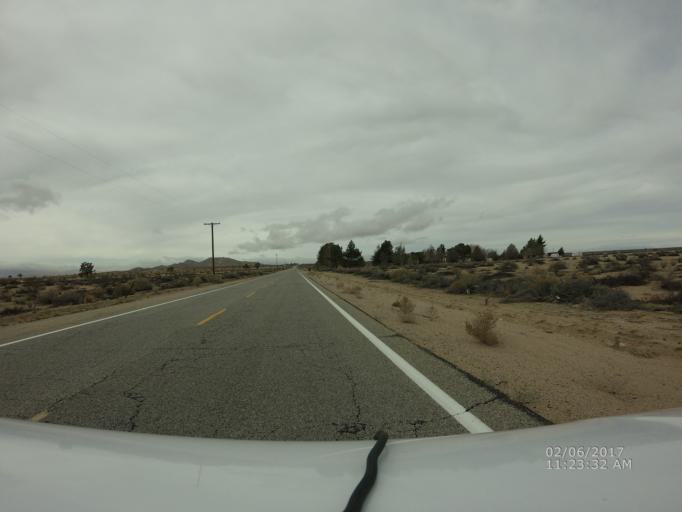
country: US
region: California
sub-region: Los Angeles County
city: Lake Los Angeles
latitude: 34.6899
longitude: -117.7417
